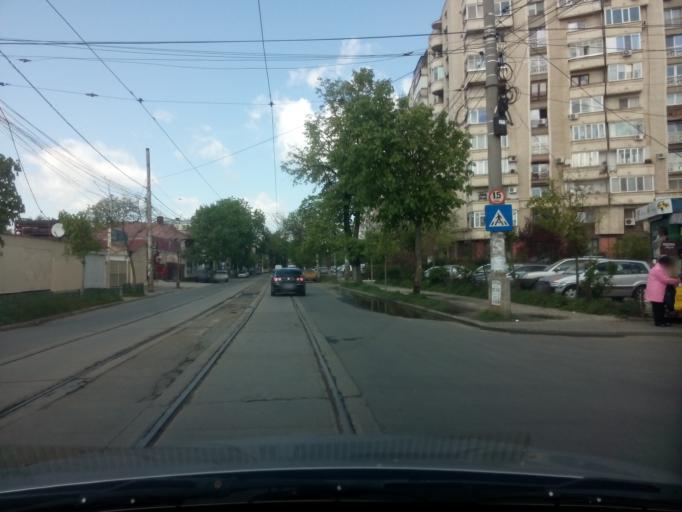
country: RO
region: Bucuresti
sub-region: Municipiul Bucuresti
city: Bucharest
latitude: 44.4557
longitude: 26.1211
